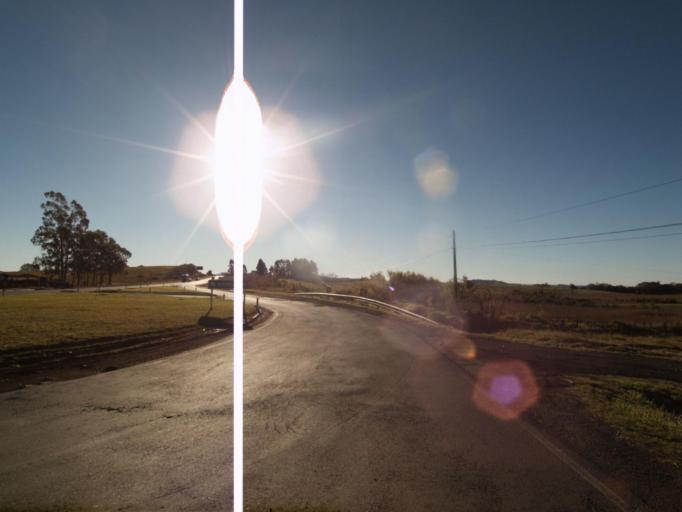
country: AR
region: Misiones
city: Bernardo de Irigoyen
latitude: -26.2870
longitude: -53.5548
